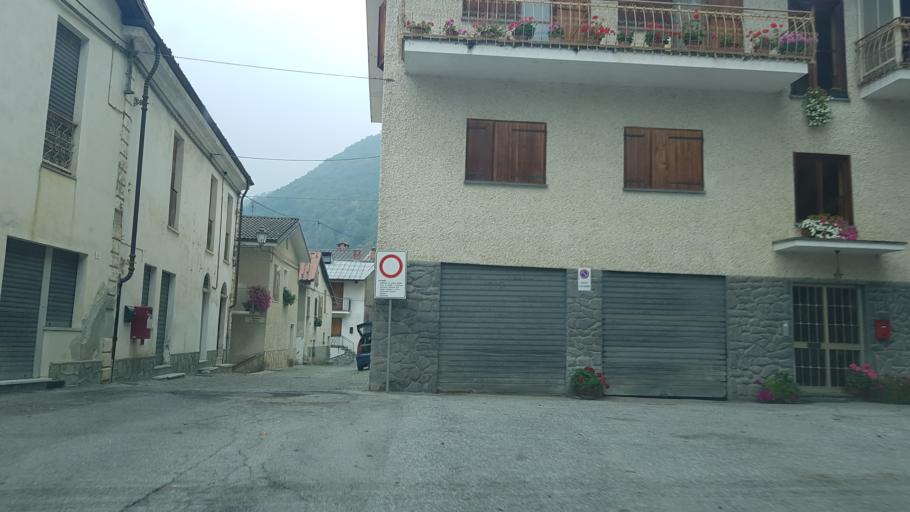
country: IT
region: Piedmont
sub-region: Provincia di Cuneo
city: Roccaforte Mondovi
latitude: 44.2793
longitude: 7.7398
